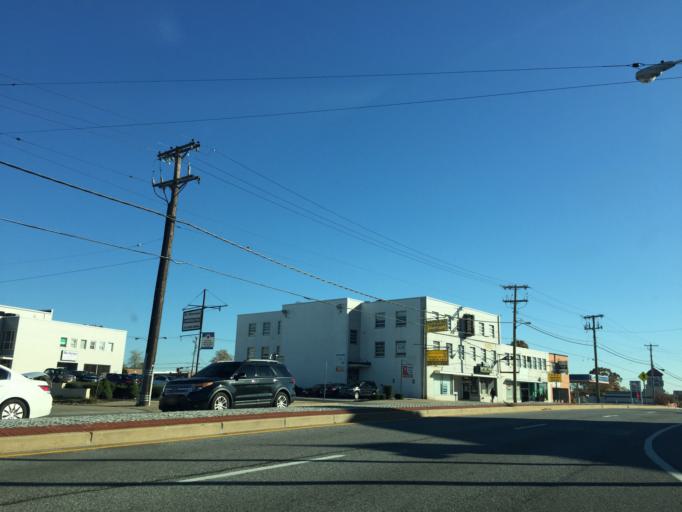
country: US
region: Maryland
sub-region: Baltimore County
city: Parkville
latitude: 39.3971
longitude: -76.5634
